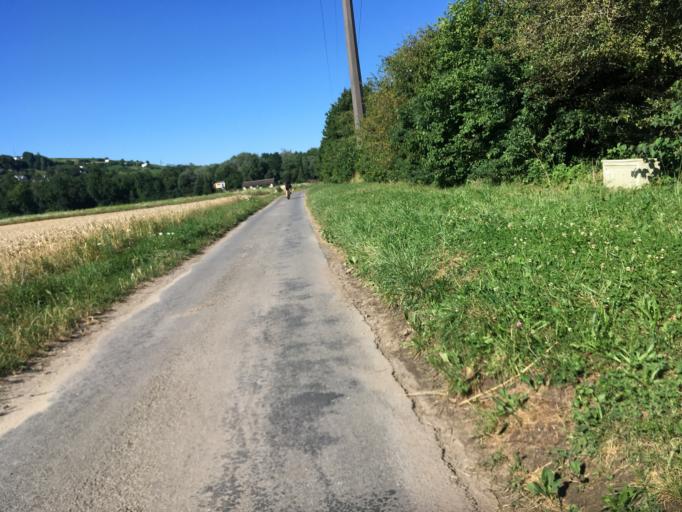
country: CH
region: Vaud
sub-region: Broye-Vully District
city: Avenches
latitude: 46.9176
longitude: 7.0283
